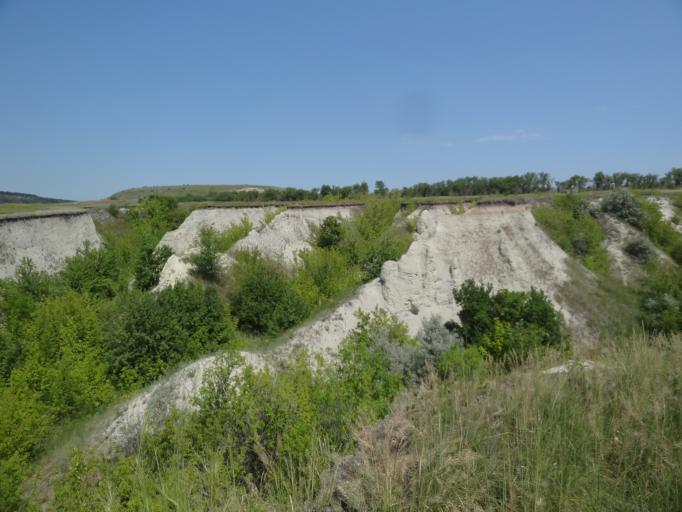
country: RU
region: Saratov
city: Sokolovyy
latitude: 51.4267
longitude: 45.8003
